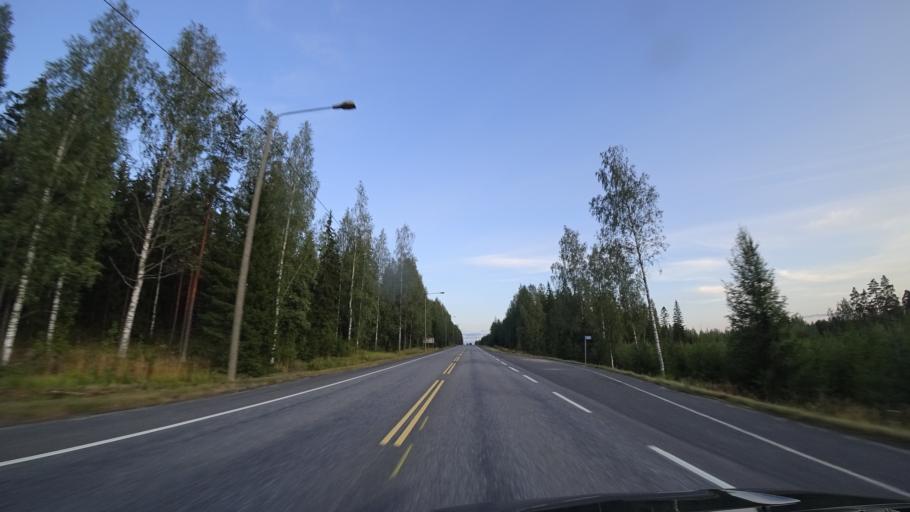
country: FI
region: Haeme
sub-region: Riihimaeki
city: Riihimaeki
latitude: 60.7489
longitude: 24.7255
